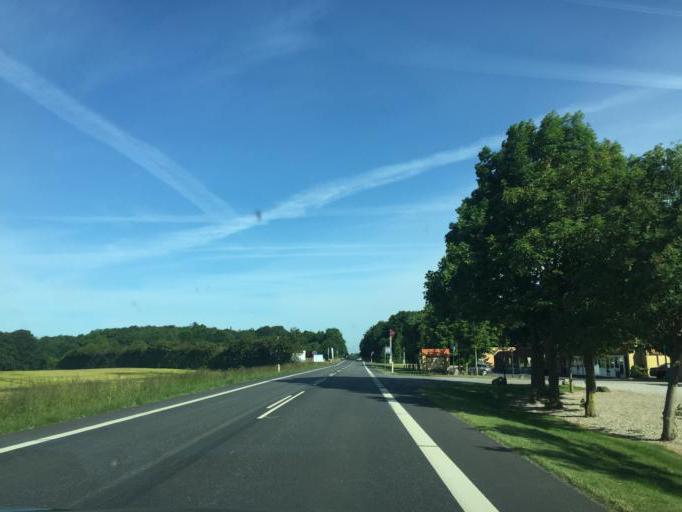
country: DK
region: South Denmark
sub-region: Middelfart Kommune
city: Brenderup
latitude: 55.4438
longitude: 9.9884
